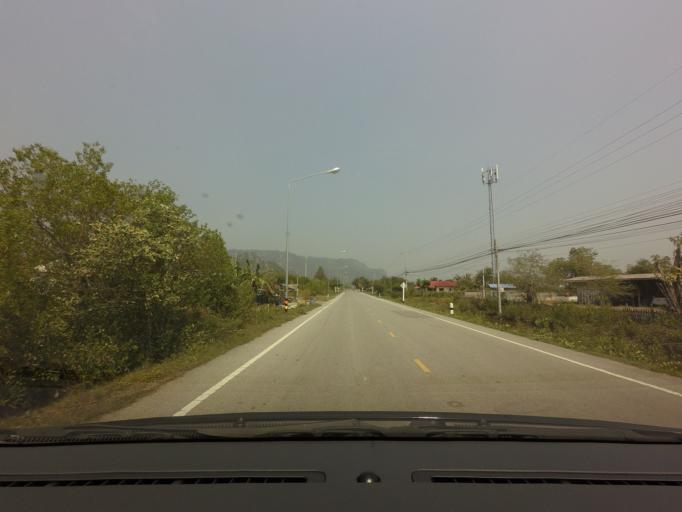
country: TH
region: Prachuap Khiri Khan
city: Kui Buri
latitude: 12.1367
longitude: 99.9638
